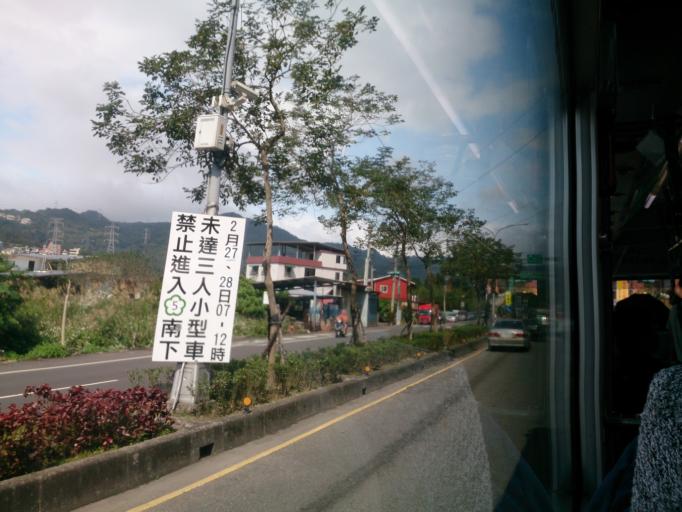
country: TW
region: Taipei
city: Taipei
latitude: 25.0022
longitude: 121.6273
